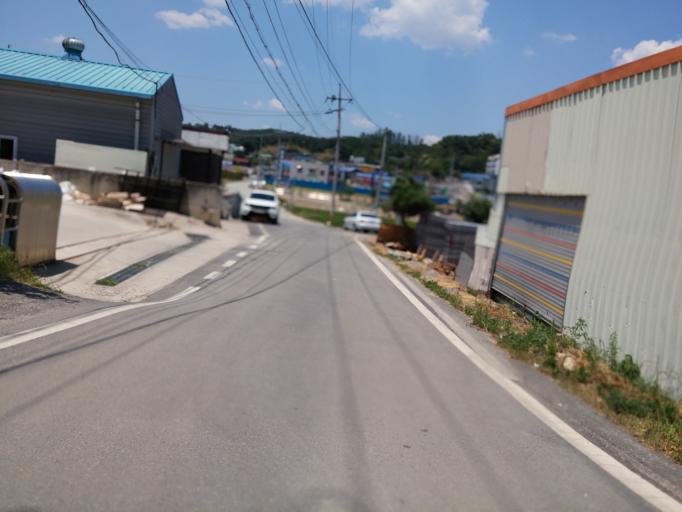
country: KR
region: Chungcheongbuk-do
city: Cheongju-si
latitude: 36.5592
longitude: 127.4377
